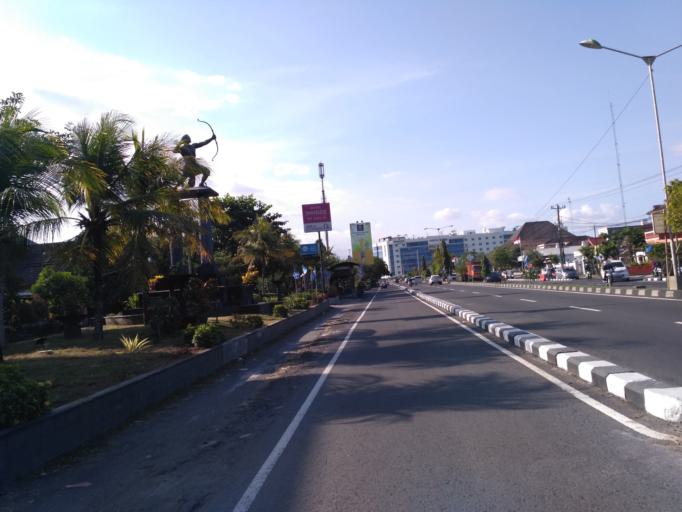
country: ID
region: Daerah Istimewa Yogyakarta
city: Depok
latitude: -7.7702
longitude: 110.4310
